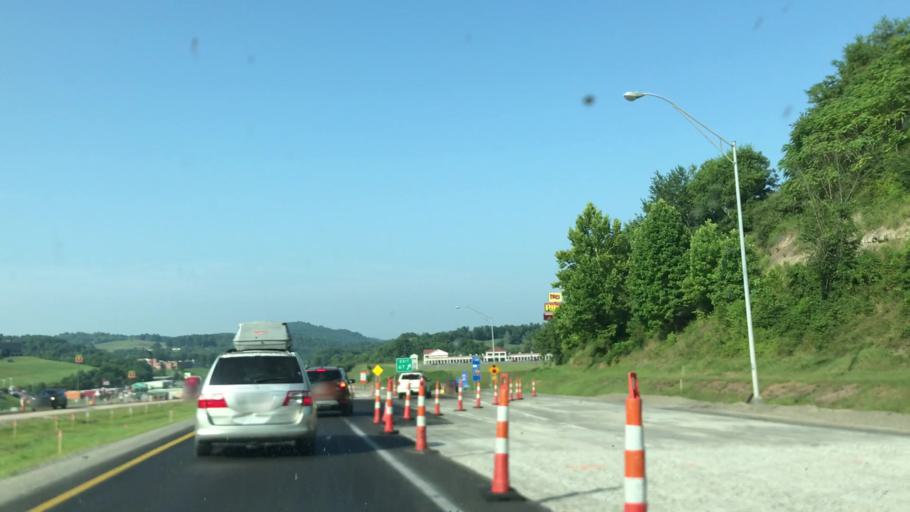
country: US
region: West Virginia
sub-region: Braxton County
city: Sutton
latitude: 38.7044
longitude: -80.6592
